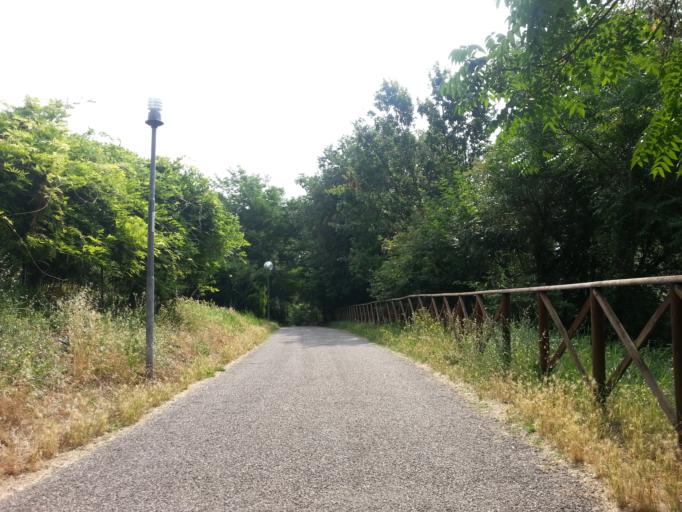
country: IT
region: Emilia-Romagna
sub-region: Provincia di Reggio Emilia
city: Reggio nell'Emilia
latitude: 44.6688
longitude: 10.6040
